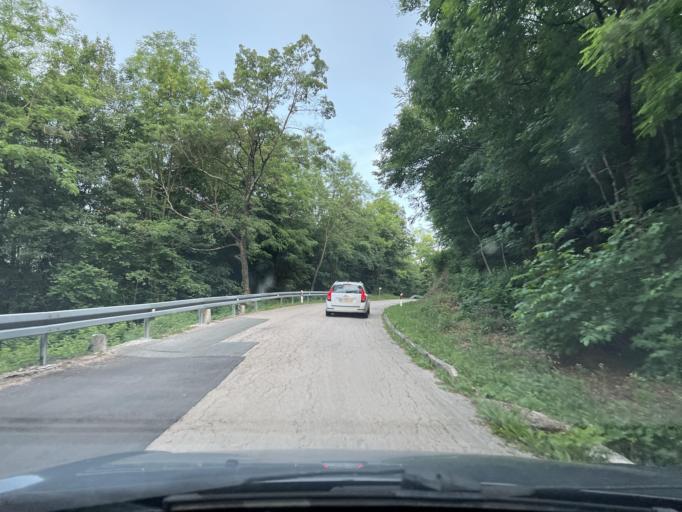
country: HR
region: Primorsko-Goranska
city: Marcelji
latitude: 45.3972
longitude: 14.4167
